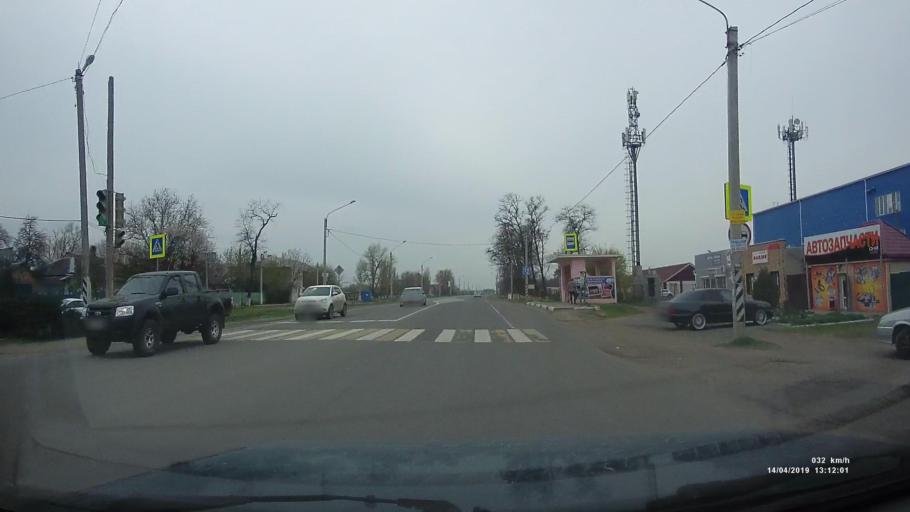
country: RU
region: Rostov
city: Kuleshovka
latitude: 47.1052
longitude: 39.6430
